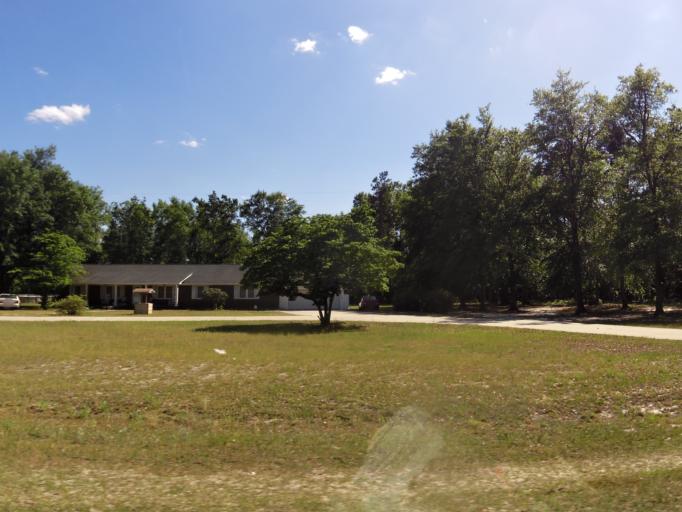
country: US
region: South Carolina
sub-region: Barnwell County
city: Williston
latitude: 33.4151
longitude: -81.4717
